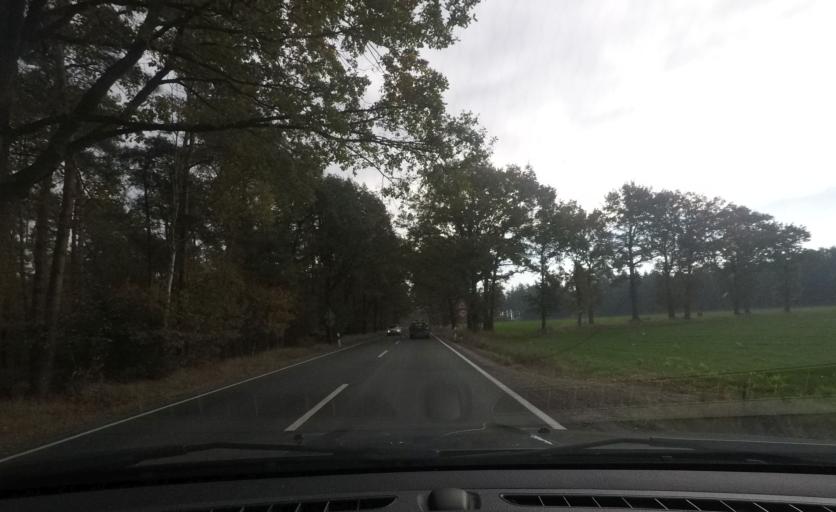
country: DE
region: North Rhine-Westphalia
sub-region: Regierungsbezirk Munster
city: Coesfeld
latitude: 51.8572
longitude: 7.1242
